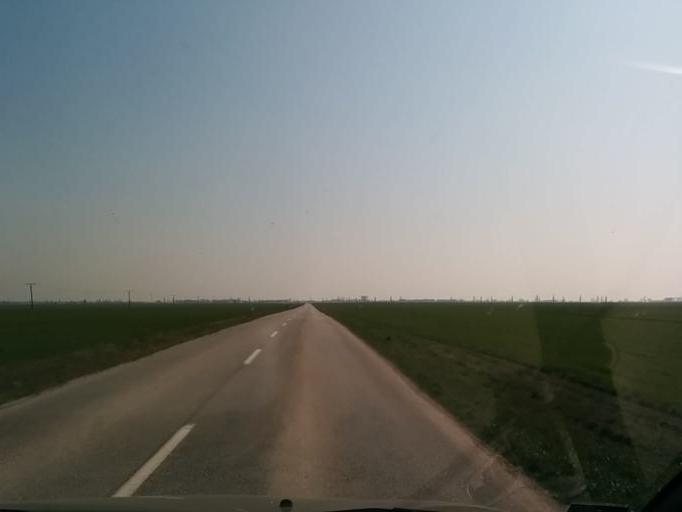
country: SK
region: Trnavsky
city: Sladkovicovo
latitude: 48.2148
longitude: 17.6007
